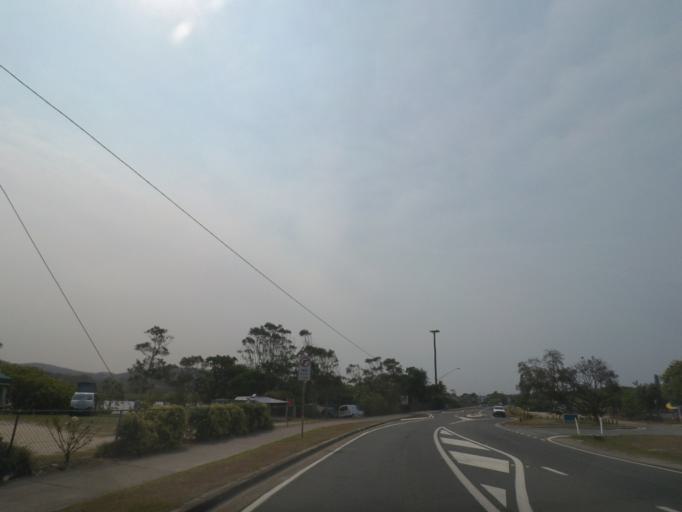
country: AU
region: New South Wales
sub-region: Tweed
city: Pottsville Beach
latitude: -28.3603
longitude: 153.5746
